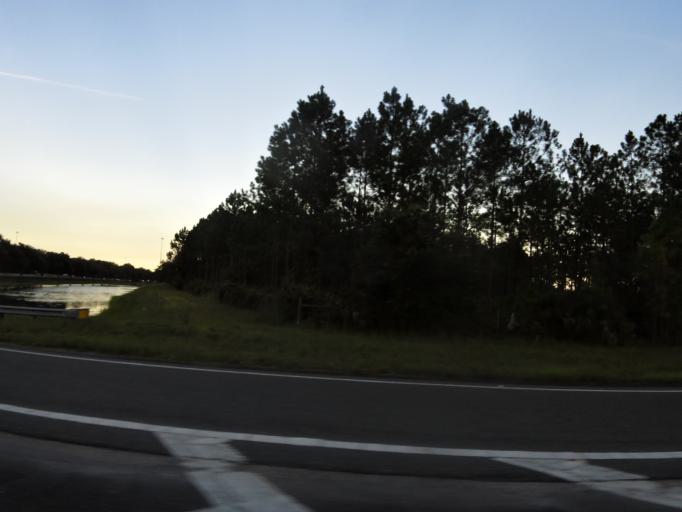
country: US
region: Florida
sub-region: Saint Johns County
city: Ponte Vedra Beach
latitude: 30.2508
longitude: -81.4989
